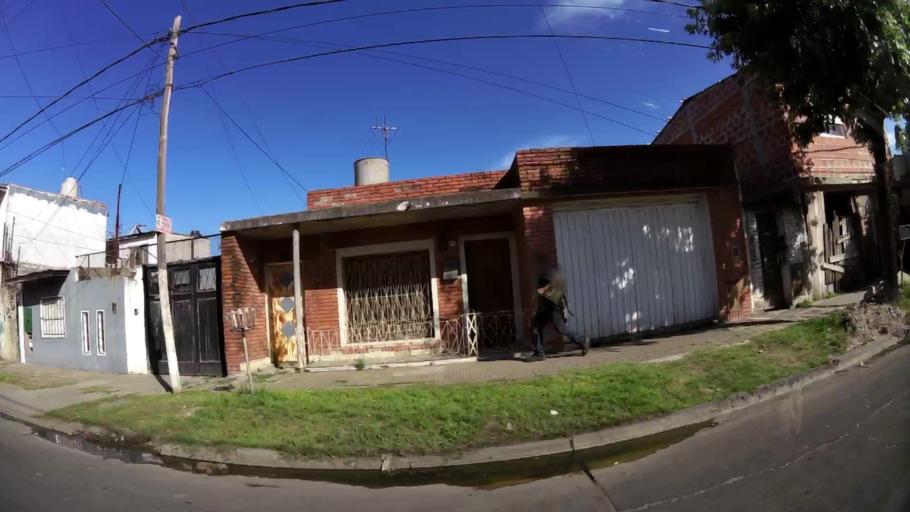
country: AR
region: Buenos Aires
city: Hurlingham
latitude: -34.5587
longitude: -58.6199
